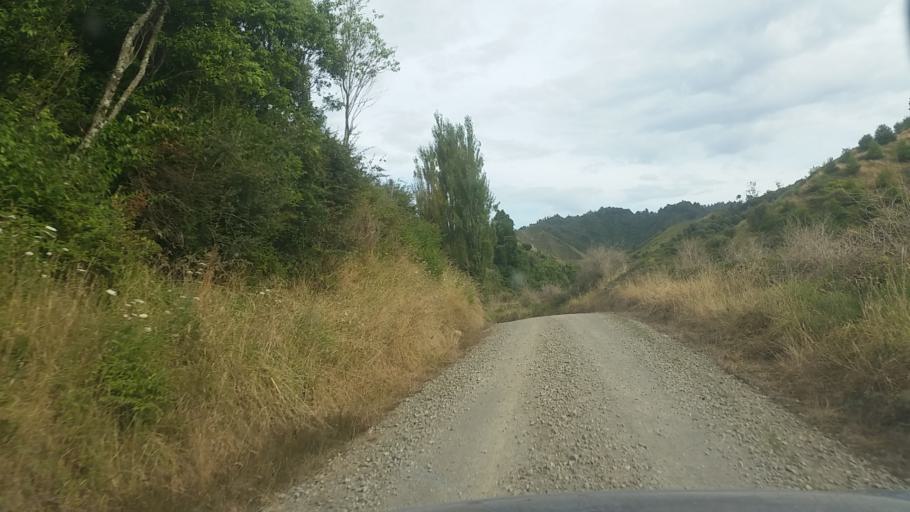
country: NZ
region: Taranaki
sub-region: New Plymouth District
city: Waitara
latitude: -39.1333
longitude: 174.7040
